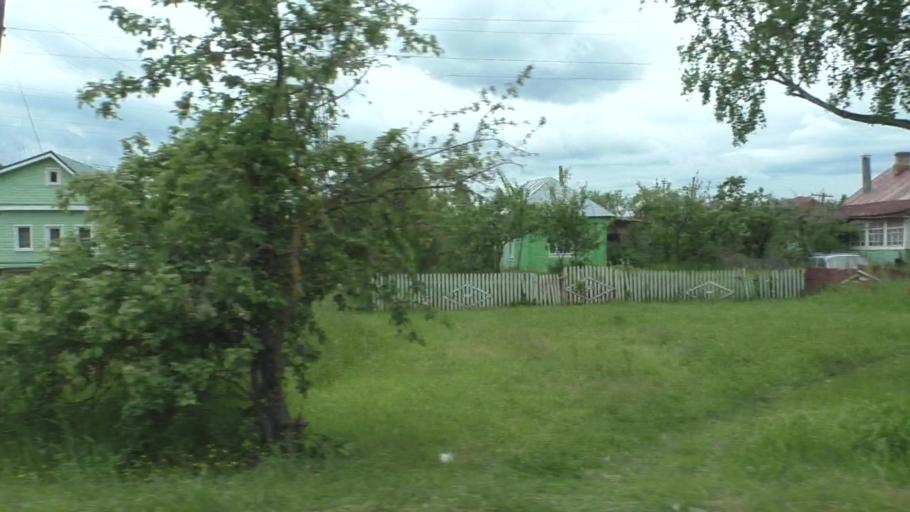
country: RU
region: Moskovskaya
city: Yegor'yevsk
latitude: 55.3978
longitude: 39.0131
